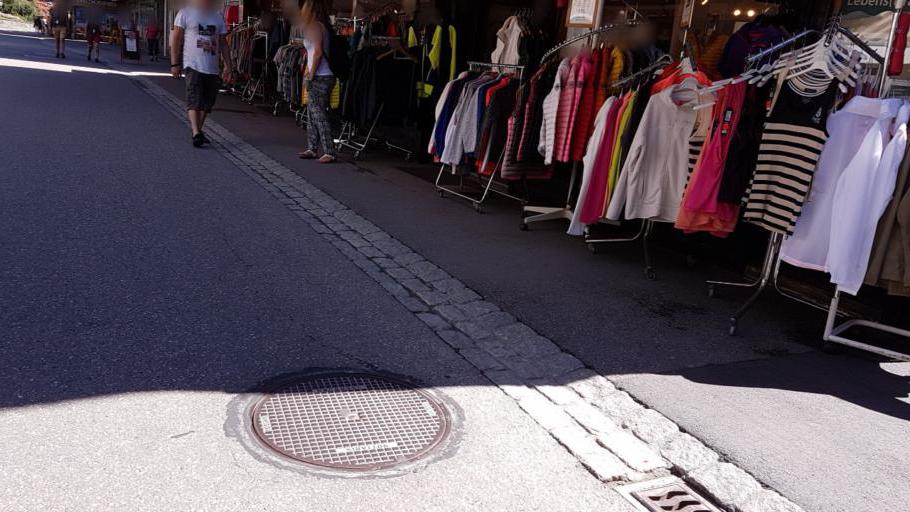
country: CH
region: Bern
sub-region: Frutigen-Niedersimmental District
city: Adelboden
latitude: 46.4918
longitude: 7.5581
